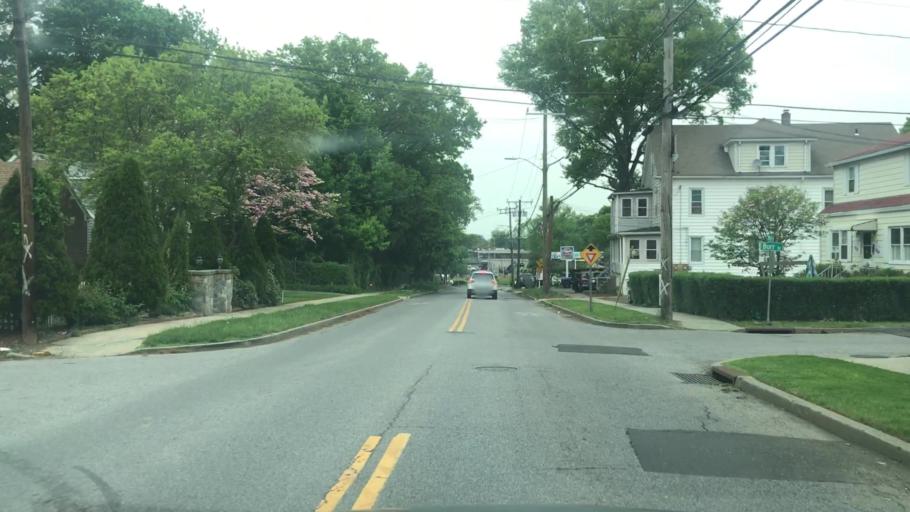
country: US
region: Connecticut
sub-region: Fairfield County
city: Stamford
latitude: 41.0521
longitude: -73.5574
